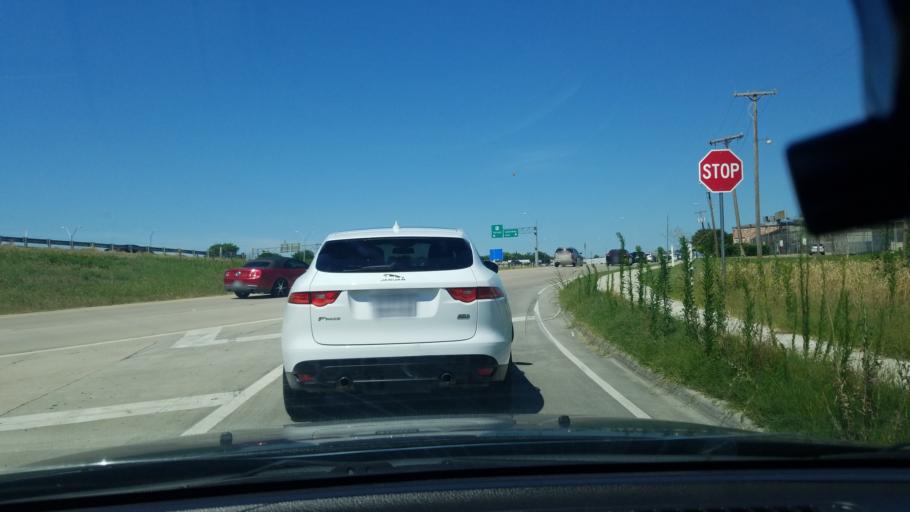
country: US
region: Texas
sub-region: Dallas County
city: Mesquite
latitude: 32.7915
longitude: -96.6231
